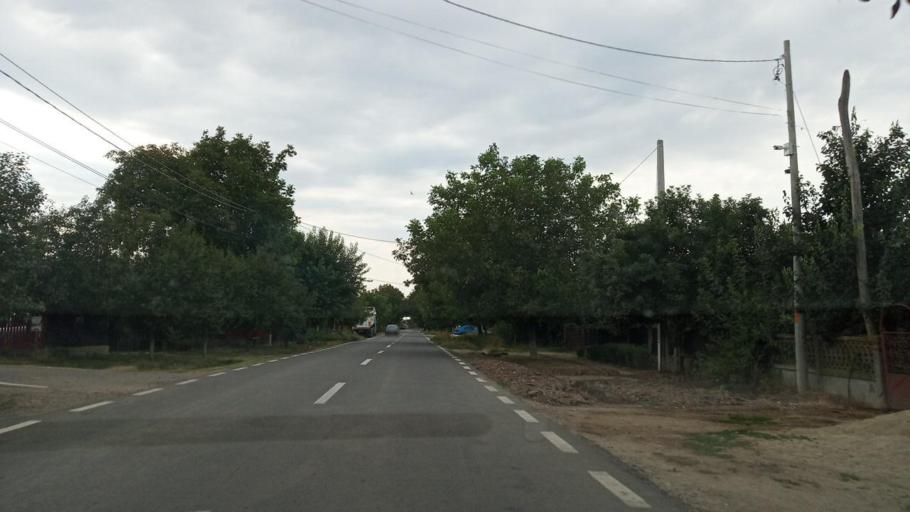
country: RO
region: Giurgiu
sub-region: Comuna Izvoarele
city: Isvoarele
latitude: 44.1669
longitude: 26.2831
